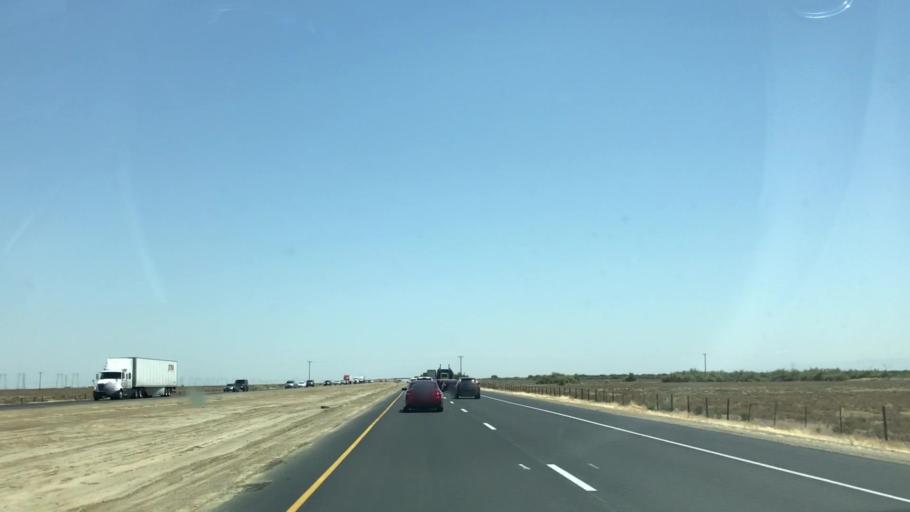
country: US
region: California
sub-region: Kern County
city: Lost Hills
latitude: 35.8073
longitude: -119.7958
